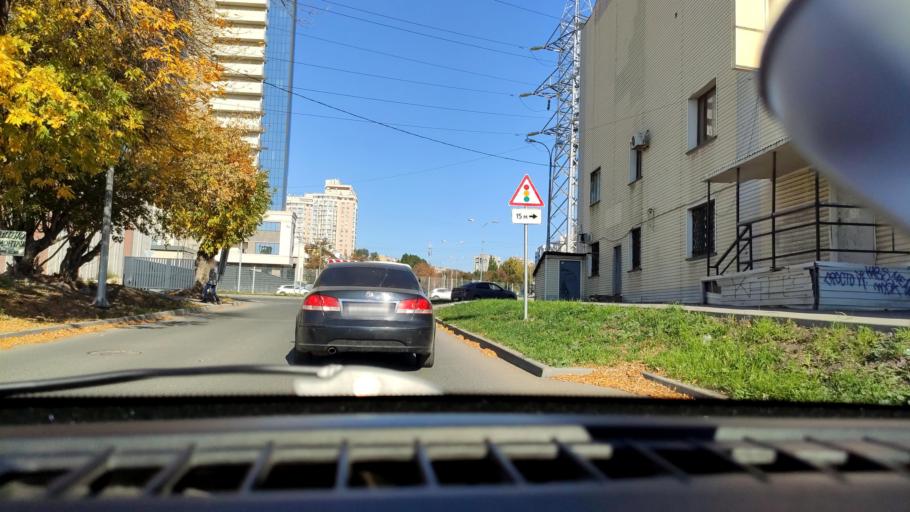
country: RU
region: Samara
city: Samara
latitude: 53.1873
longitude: 50.1333
